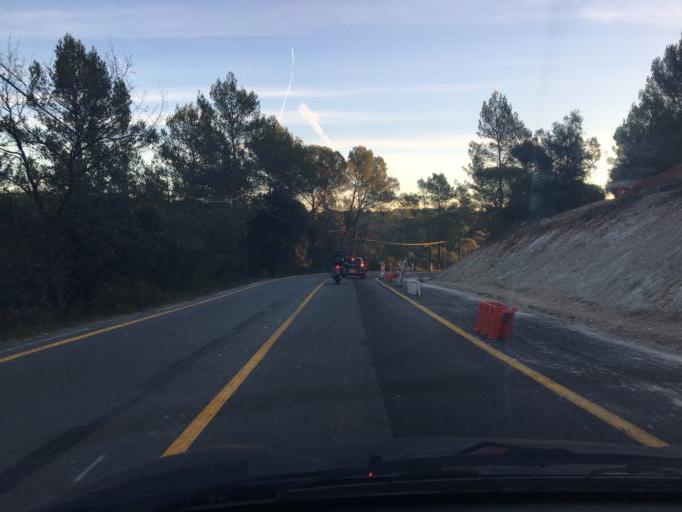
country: FR
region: Provence-Alpes-Cote d'Azur
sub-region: Departement du Var
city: Taradeau
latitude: 43.4606
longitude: 6.4134
